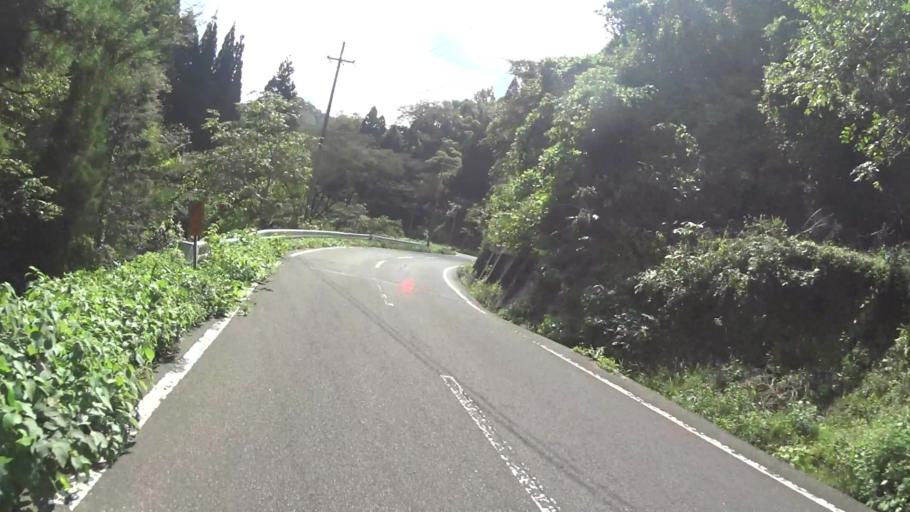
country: JP
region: Kyoto
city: Miyazu
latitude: 35.6884
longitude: 135.1576
